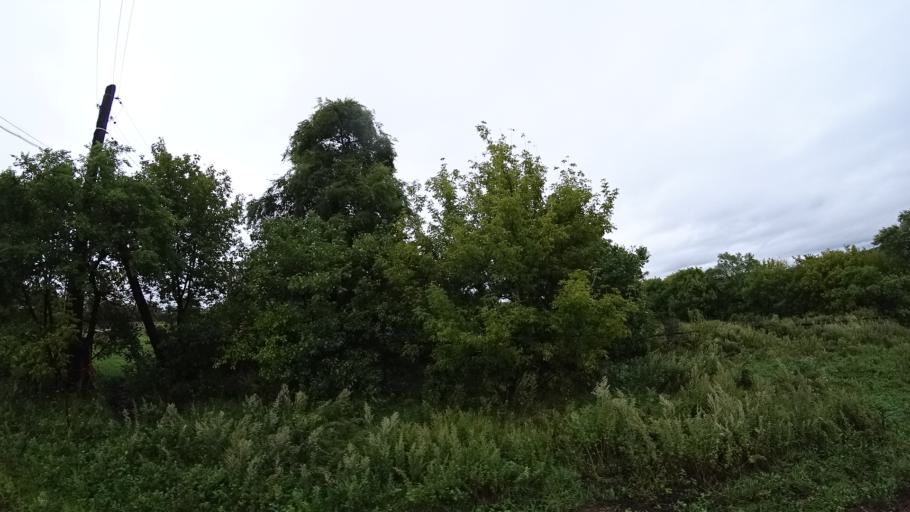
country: RU
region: Primorskiy
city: Monastyrishche
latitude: 44.2644
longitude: 132.4208
